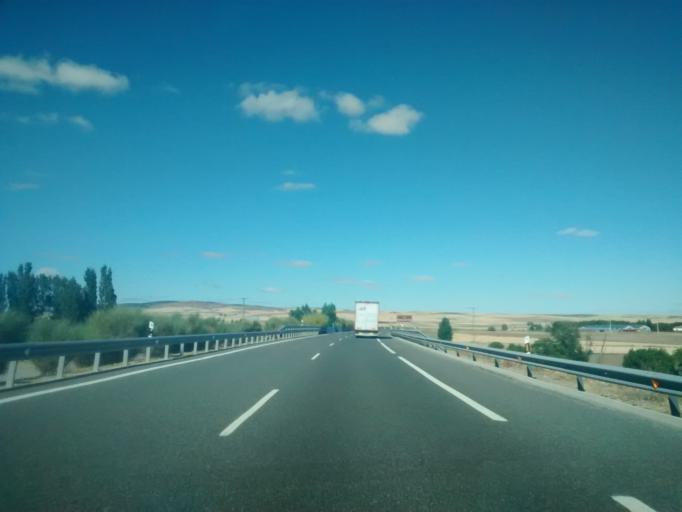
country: ES
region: Castille and Leon
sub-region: Provincia de Avila
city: San Pedro del Arroyo
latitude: 40.8079
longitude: -4.8858
